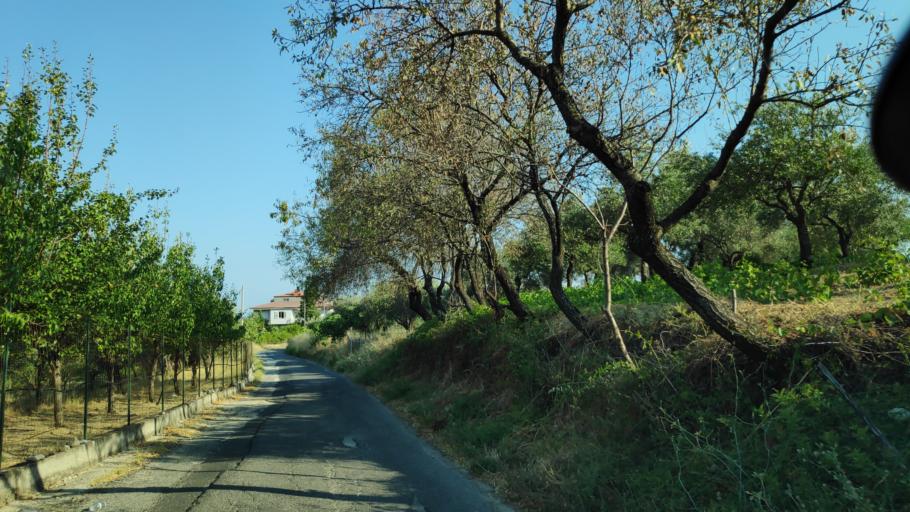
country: IT
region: Calabria
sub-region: Provincia di Catanzaro
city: Guardavalle
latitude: 38.5106
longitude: 16.5036
